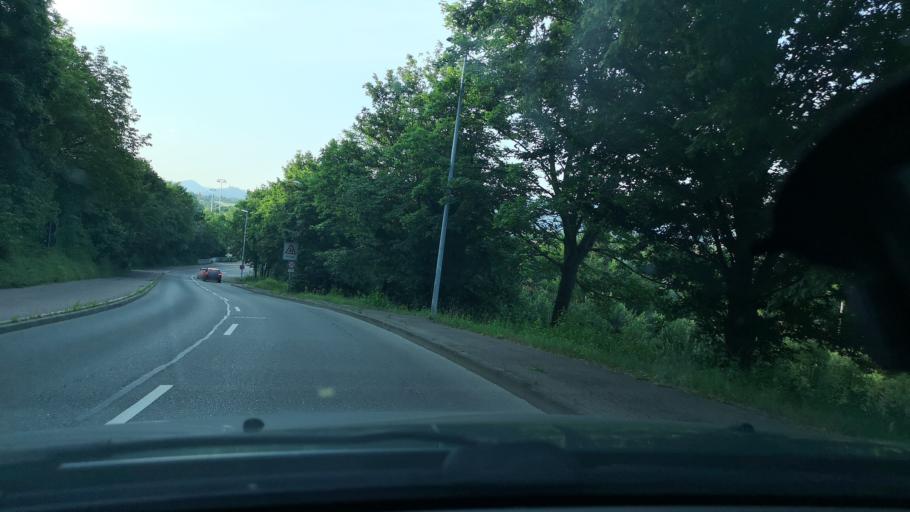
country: DE
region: Baden-Wuerttemberg
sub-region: Regierungsbezirk Stuttgart
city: Kirchheim unter Teck
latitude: 48.6458
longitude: 9.4661
